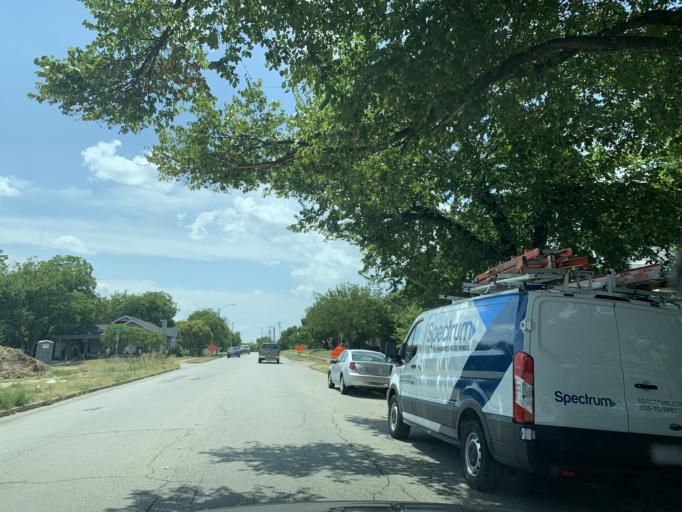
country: US
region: Texas
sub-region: Tarrant County
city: Fort Worth
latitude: 32.7130
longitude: -97.3226
